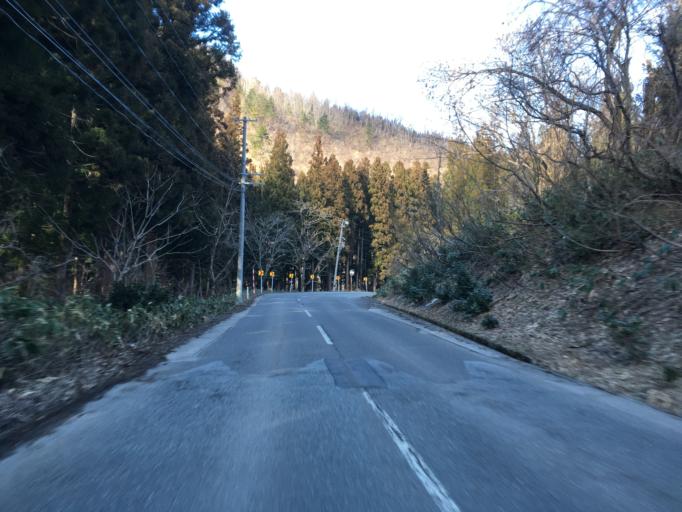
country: JP
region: Yamagata
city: Nagai
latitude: 37.9798
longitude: 139.9348
